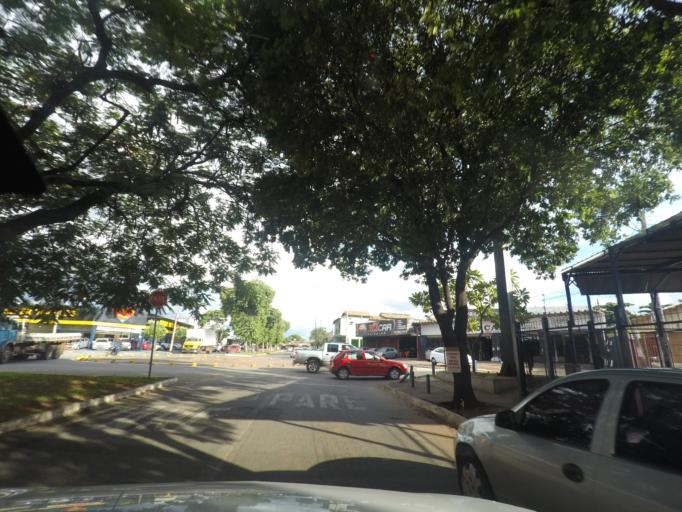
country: BR
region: Goias
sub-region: Goiania
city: Goiania
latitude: -16.6890
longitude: -49.3059
